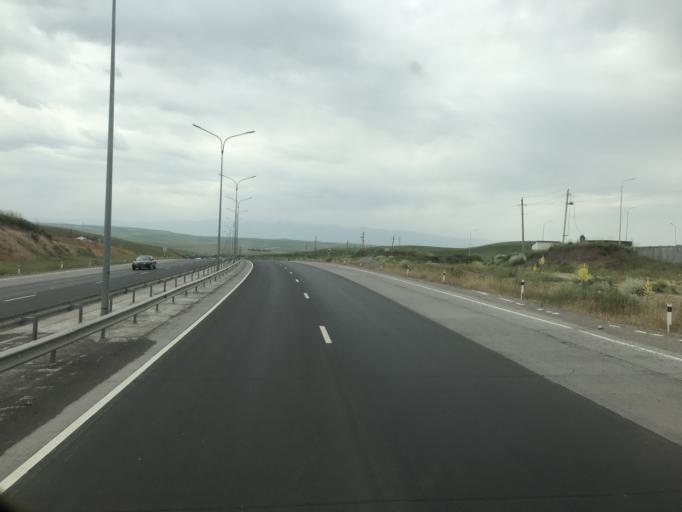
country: KZ
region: Ongtustik Qazaqstan
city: Qazyqurt
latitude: 41.9949
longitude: 69.4785
